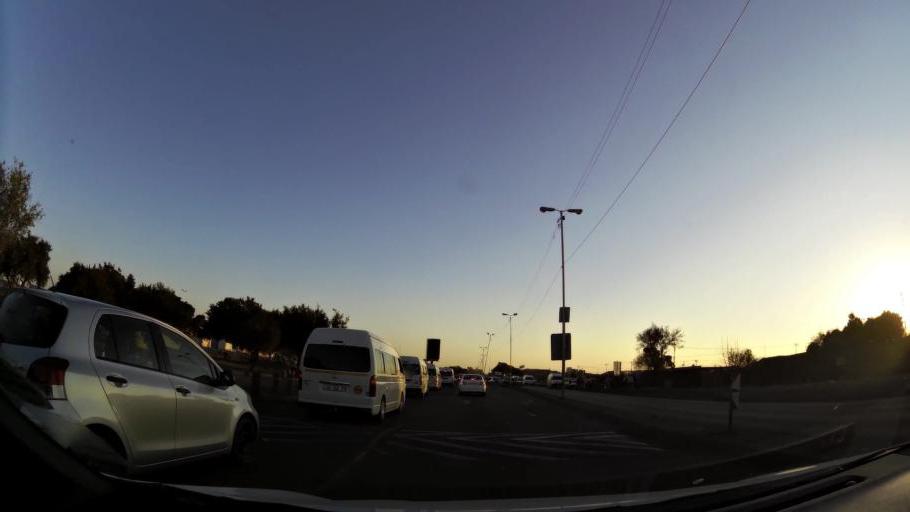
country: ZA
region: Gauteng
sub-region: City of Tshwane Metropolitan Municipality
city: Cullinan
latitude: -25.7166
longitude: 28.3698
